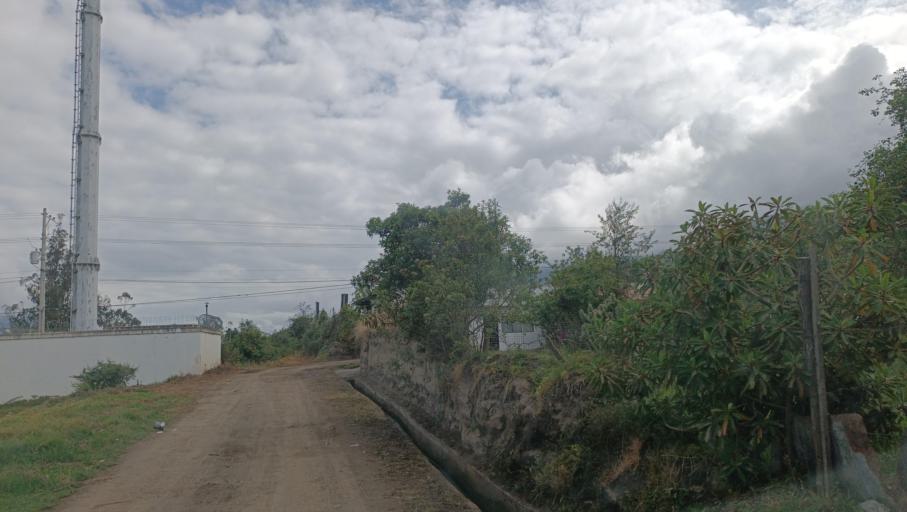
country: EC
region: Chimborazo
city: Guano
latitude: -1.6573
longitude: -78.5689
